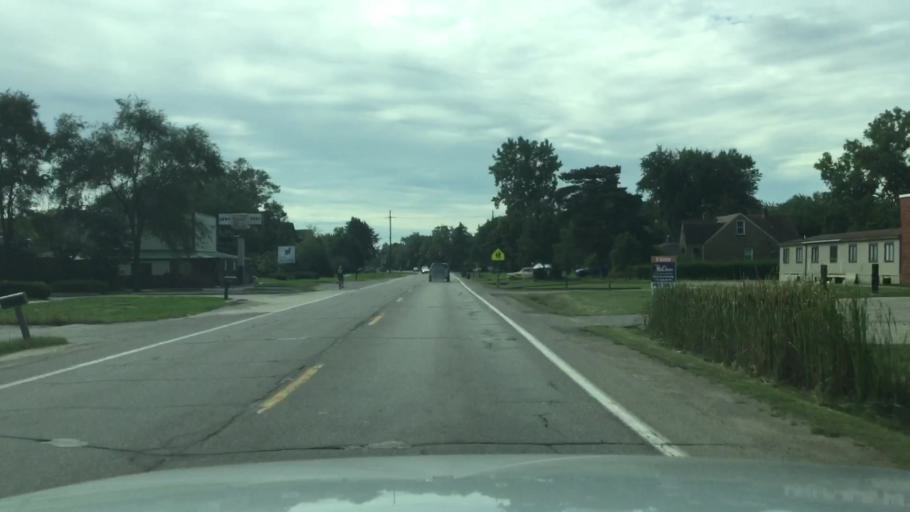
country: US
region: Michigan
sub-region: Wayne County
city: Belleville
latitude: 42.2000
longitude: -83.4851
